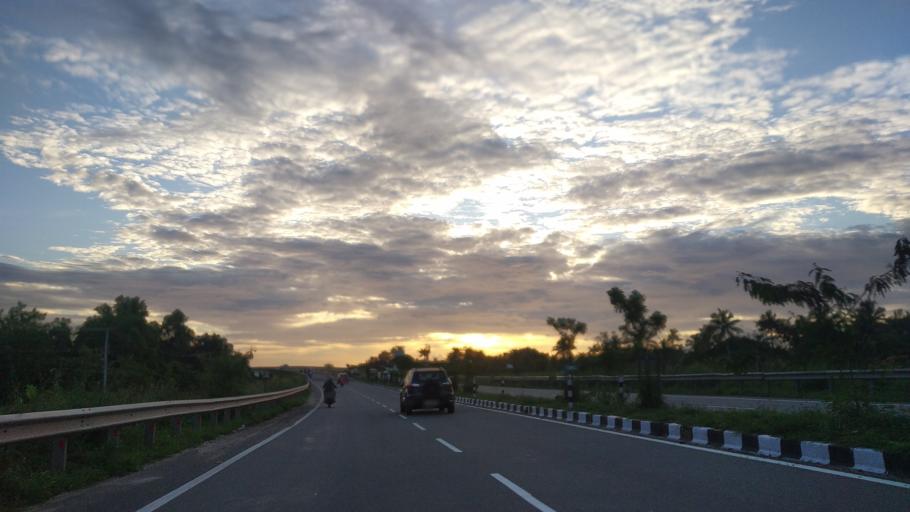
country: IN
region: Kerala
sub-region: Ernakulam
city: Elur
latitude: 10.0486
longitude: 76.2703
